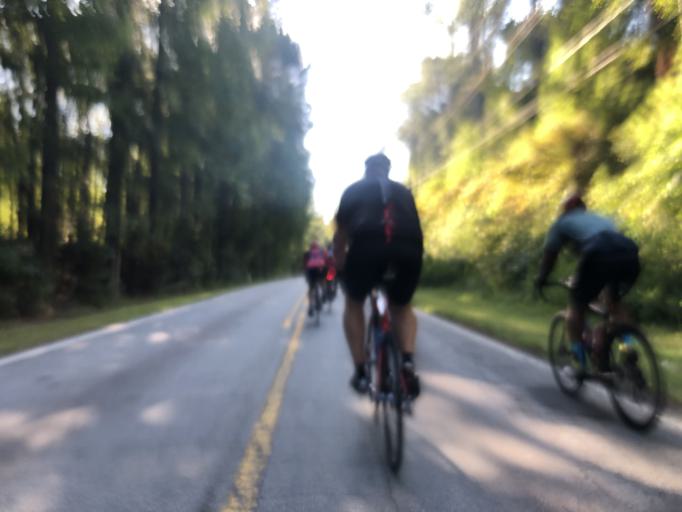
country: US
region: Georgia
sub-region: Fulton County
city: Chattahoochee Hills
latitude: 33.5492
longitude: -84.7635
